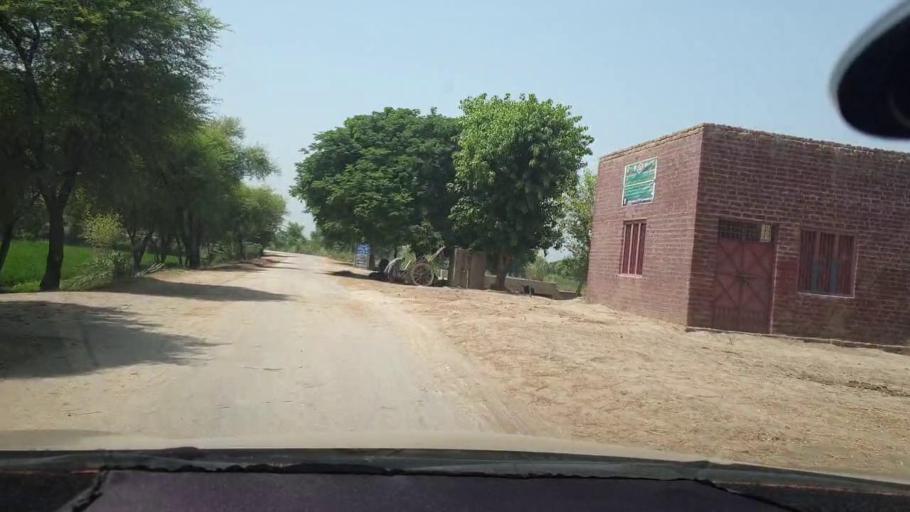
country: PK
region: Sindh
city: Kambar
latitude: 27.6637
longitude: 67.9455
